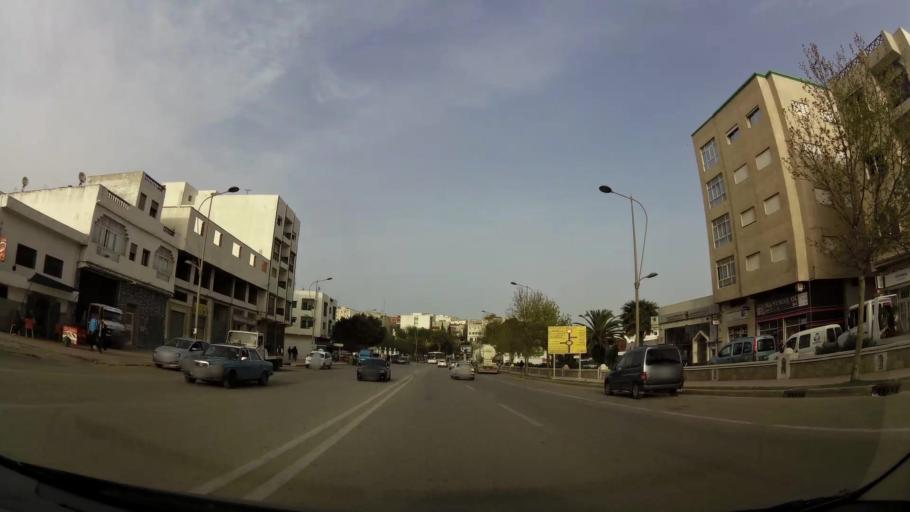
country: MA
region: Tanger-Tetouan
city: Tetouan
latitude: 35.5653
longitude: -5.3999
